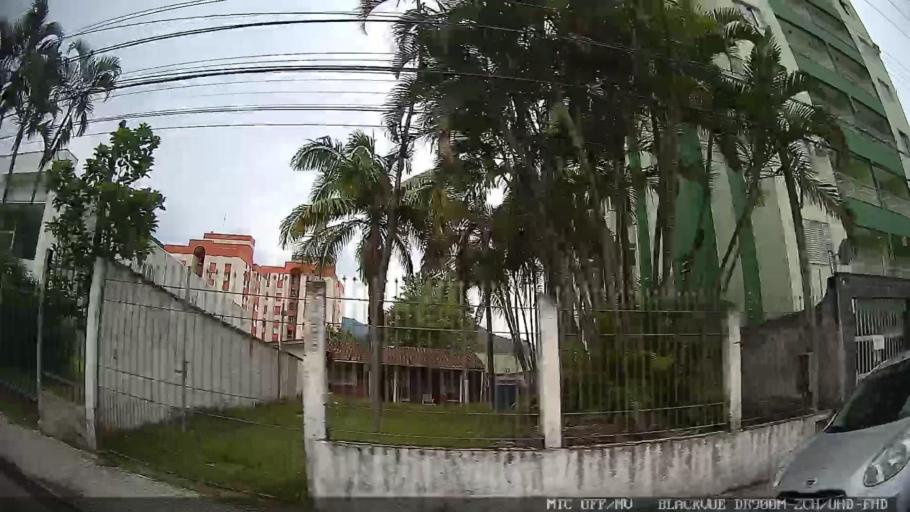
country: BR
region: Sao Paulo
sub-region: Caraguatatuba
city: Caraguatatuba
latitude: -23.6229
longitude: -45.4002
